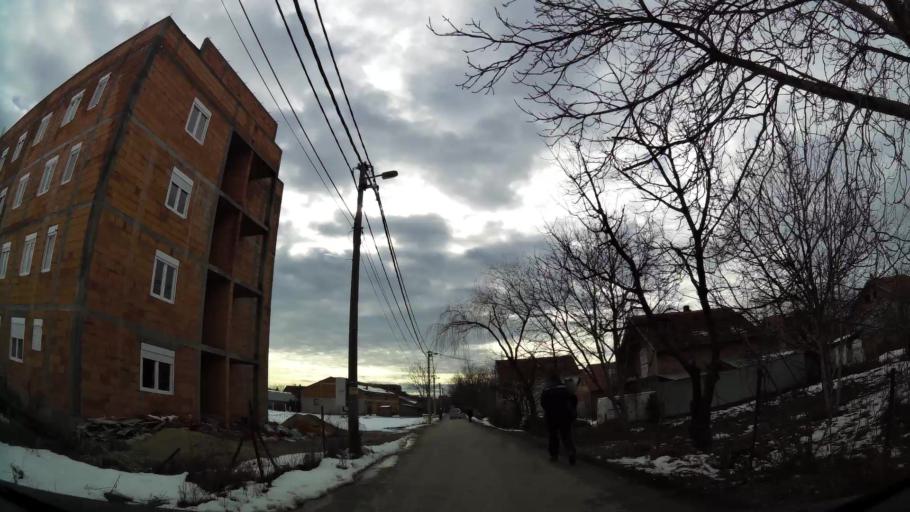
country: RS
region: Central Serbia
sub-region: Belgrade
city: Surcin
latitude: 44.8034
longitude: 20.3347
